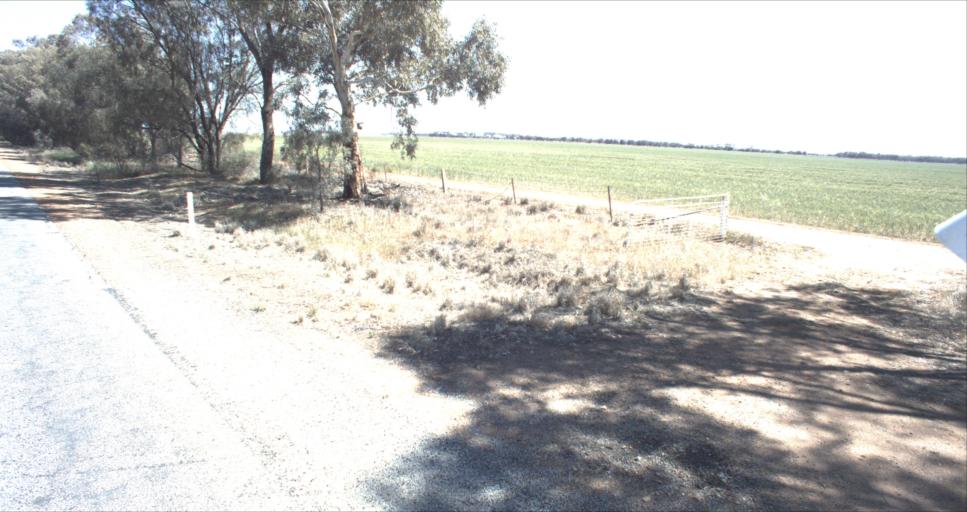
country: AU
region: New South Wales
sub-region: Leeton
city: Leeton
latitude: -34.5781
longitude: 146.2662
